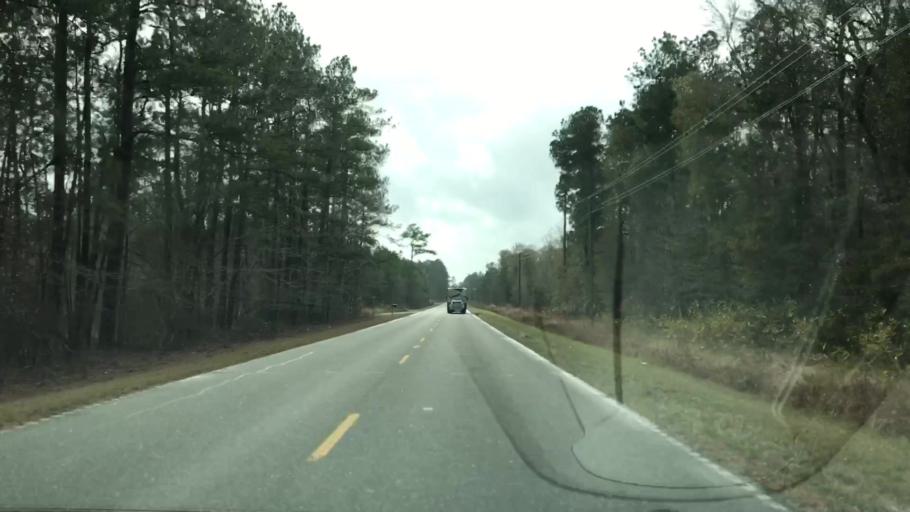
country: US
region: South Carolina
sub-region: Georgetown County
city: Murrells Inlet
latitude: 33.6285
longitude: -79.1895
